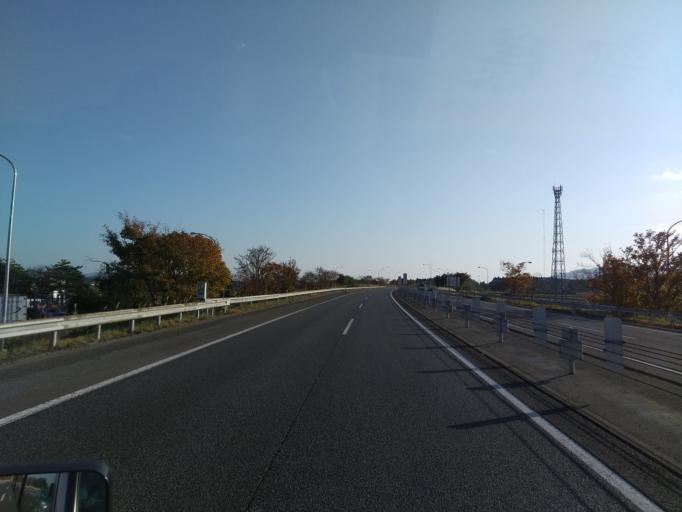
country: JP
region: Iwate
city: Morioka-shi
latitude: 39.6189
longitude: 141.1300
